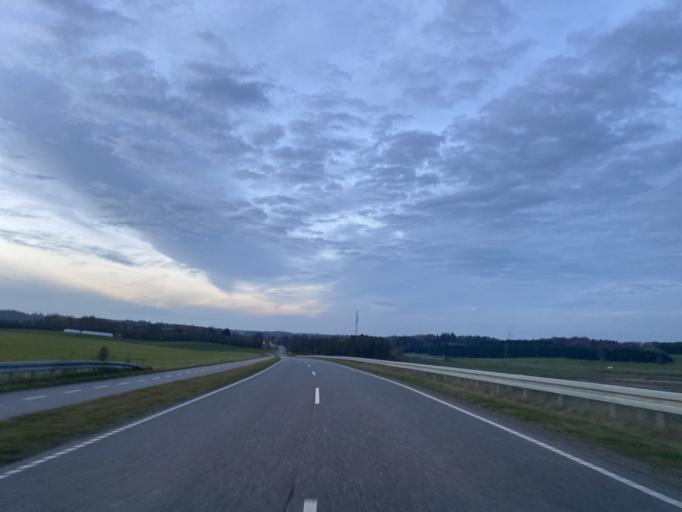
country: DK
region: Central Jutland
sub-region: Silkeborg Kommune
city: Svejbaek
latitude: 56.1475
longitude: 9.7036
